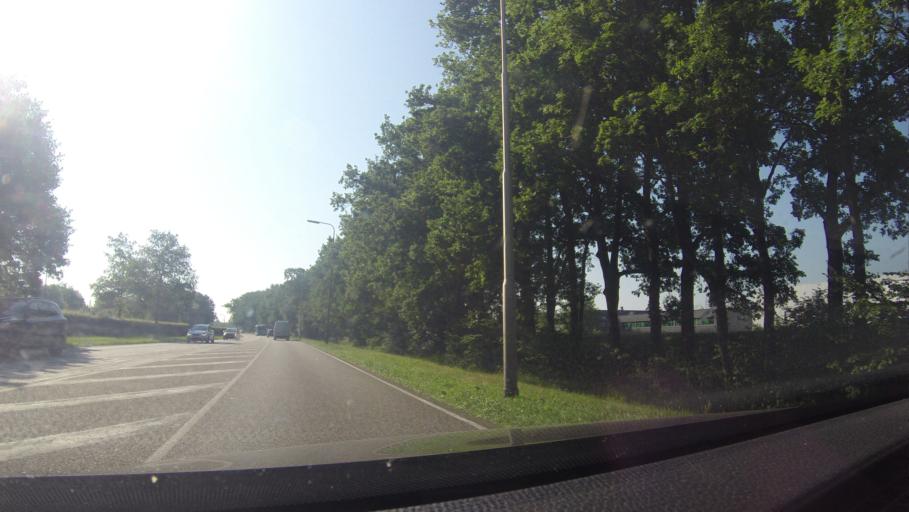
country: NL
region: Overijssel
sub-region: Gemeente Zwolle
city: Zwolle
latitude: 52.4935
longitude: 6.1422
